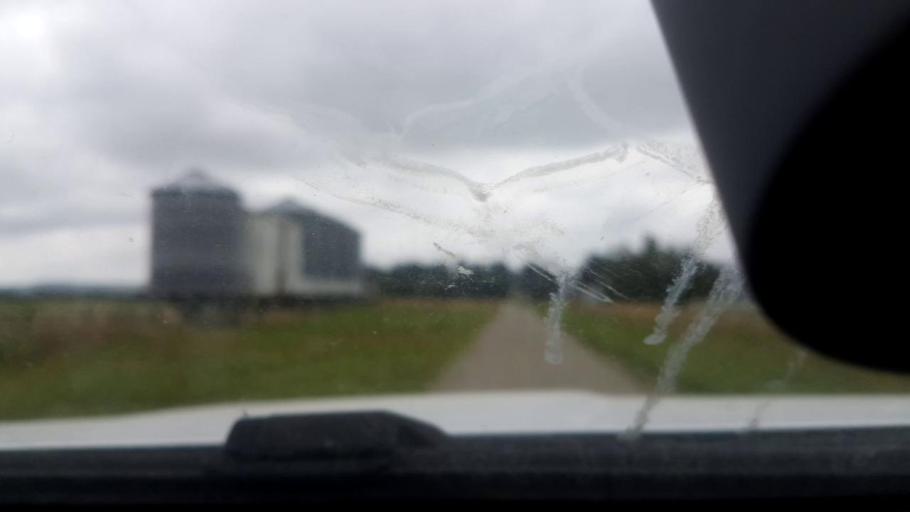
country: NZ
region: Canterbury
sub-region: Timaru District
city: Pleasant Point
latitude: -44.2251
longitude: 171.1642
